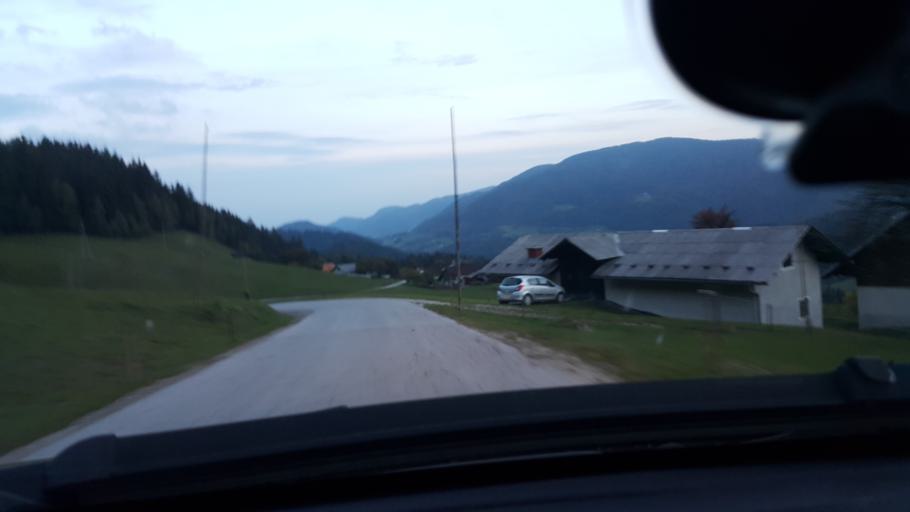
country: SI
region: Vitanje
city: Vitanje
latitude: 46.4104
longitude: 15.2821
